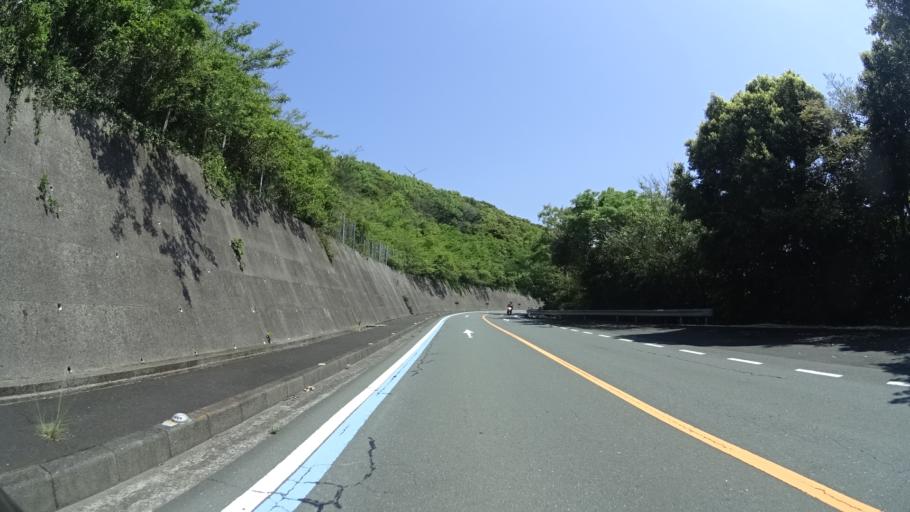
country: JP
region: Ehime
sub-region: Nishiuwa-gun
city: Ikata-cho
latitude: 33.4648
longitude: 132.2727
